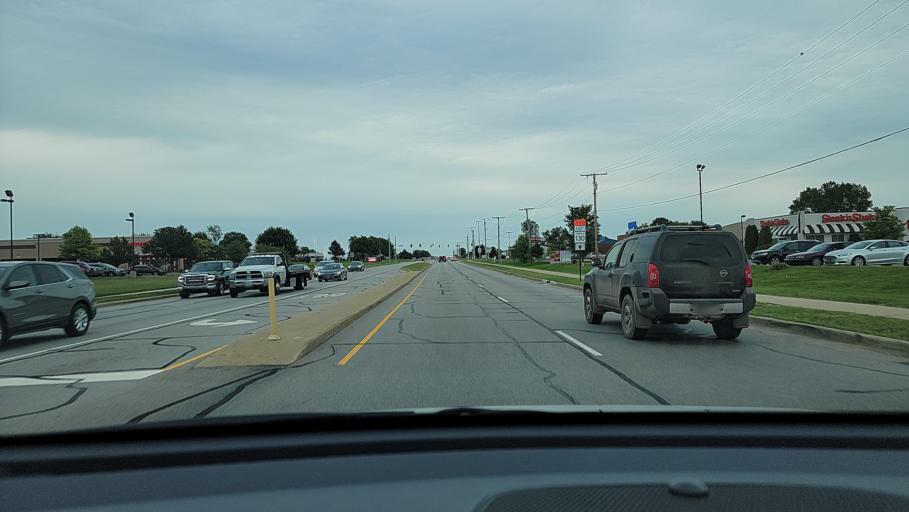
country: US
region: Indiana
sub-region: Porter County
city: Portage
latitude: 41.5505
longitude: -87.1750
